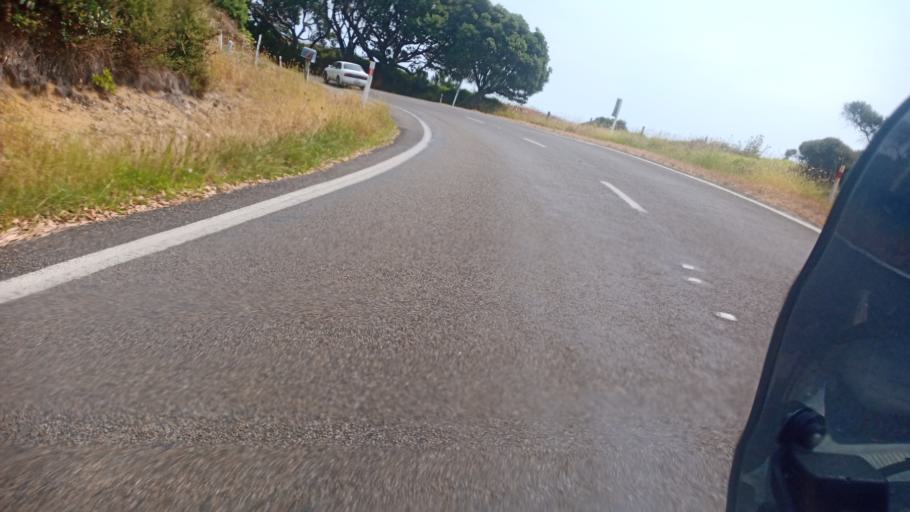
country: NZ
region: Bay of Plenty
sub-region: Opotiki District
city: Opotiki
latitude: -37.5910
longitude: 177.9780
